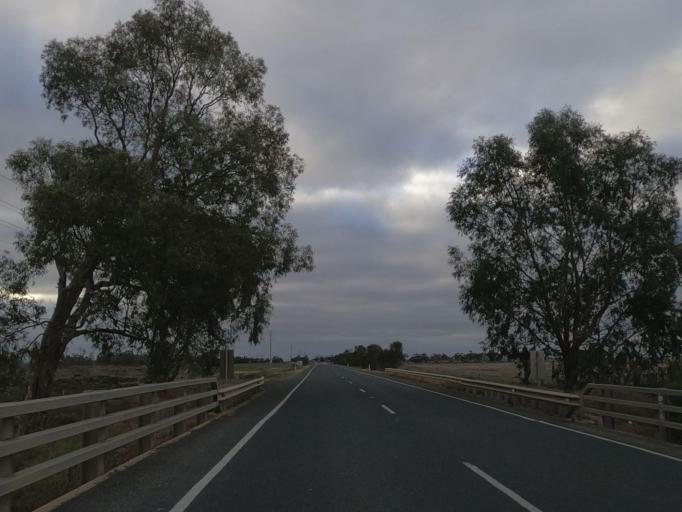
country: AU
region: Victoria
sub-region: Swan Hill
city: Swan Hill
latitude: -35.6190
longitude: 143.8034
